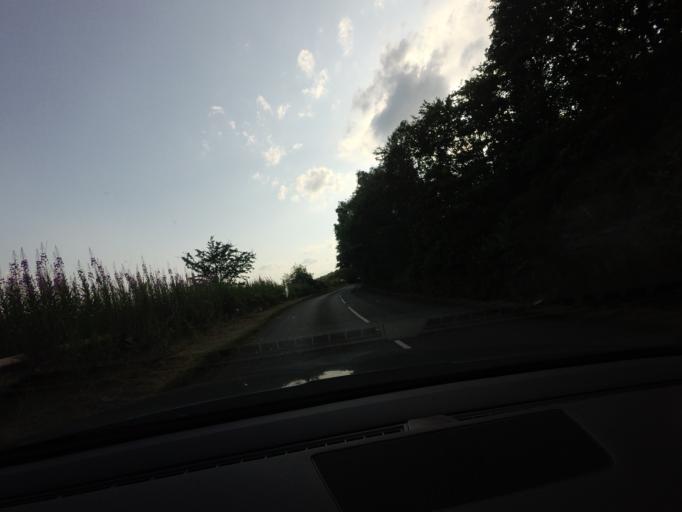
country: GB
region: Scotland
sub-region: Highland
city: Evanton
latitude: 57.6250
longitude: -4.3770
